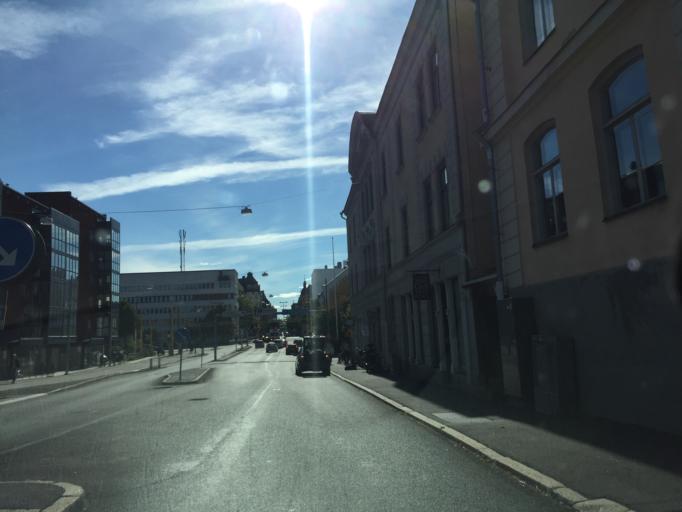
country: SE
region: OErebro
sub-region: Orebro Kommun
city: Orebro
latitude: 59.2796
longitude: 15.2180
